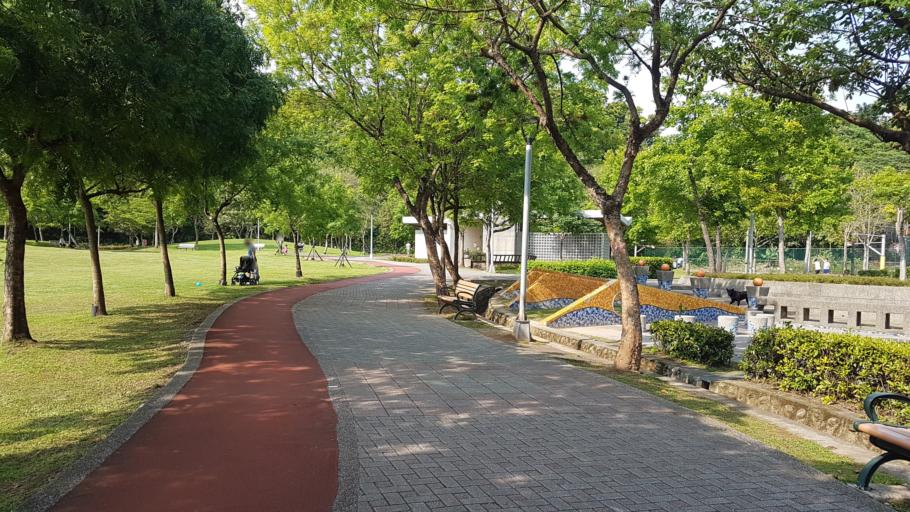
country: TW
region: Taipei
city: Taipei
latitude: 25.0023
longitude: 121.5439
